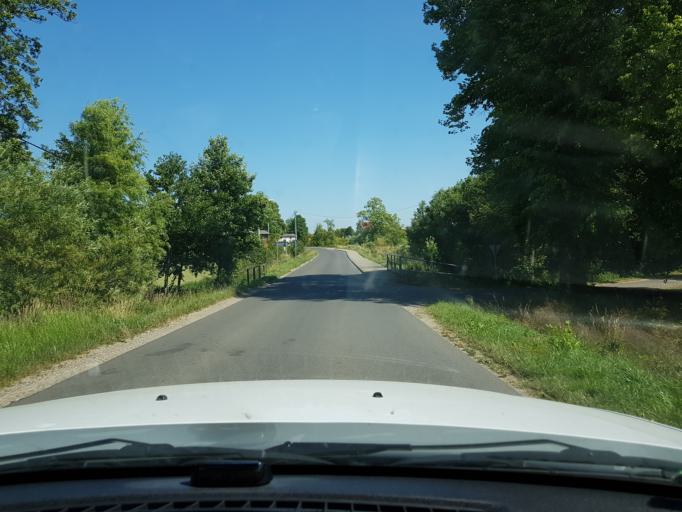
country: PL
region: West Pomeranian Voivodeship
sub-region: Powiat koszalinski
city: Mielno
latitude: 54.1876
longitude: 16.0660
